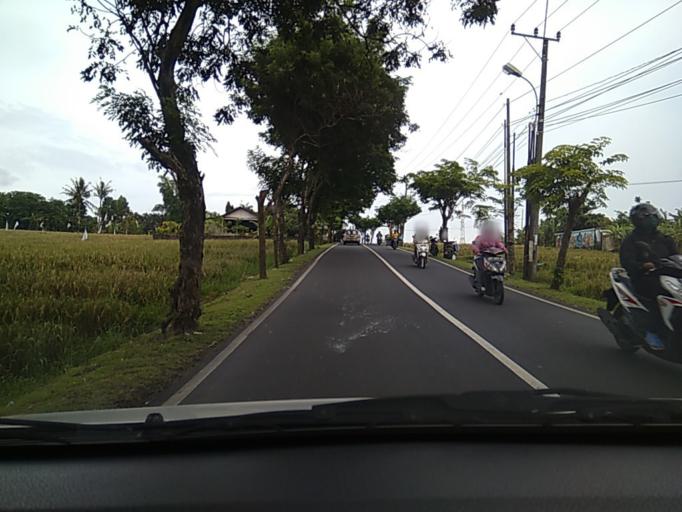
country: ID
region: Bali
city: Banjar Gunungpande
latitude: -8.6357
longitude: 115.1424
